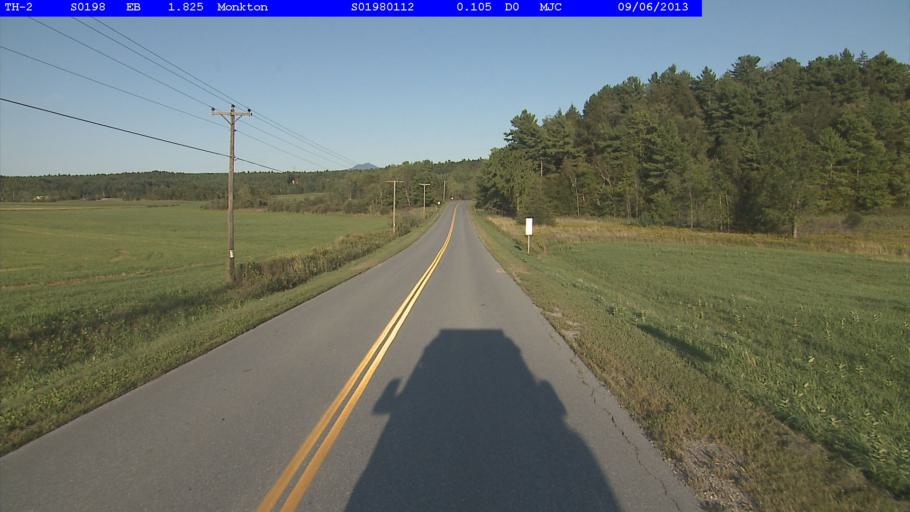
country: US
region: Vermont
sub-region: Addison County
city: Vergennes
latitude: 44.2552
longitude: -73.1929
